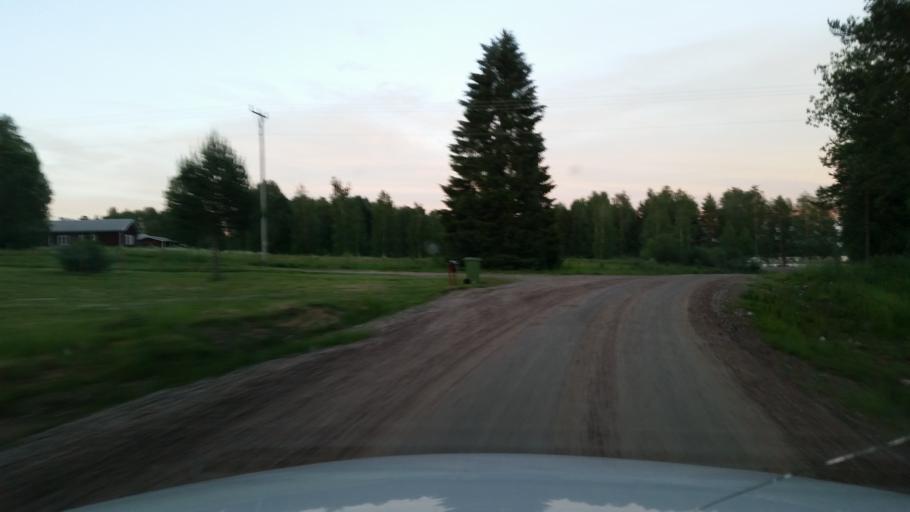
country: SE
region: Vaesternorrland
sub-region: Ange Kommun
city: Ange
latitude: 62.1845
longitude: 15.6361
